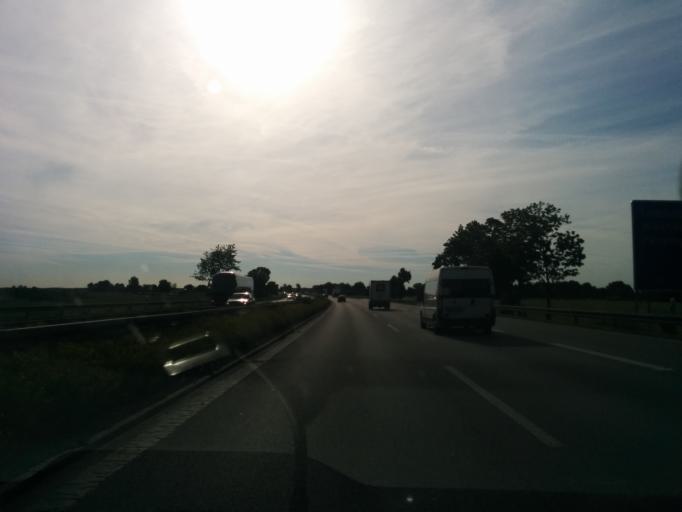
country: DE
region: Bavaria
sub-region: Upper Bavaria
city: Landsberg am Lech
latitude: 48.0569
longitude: 10.8979
